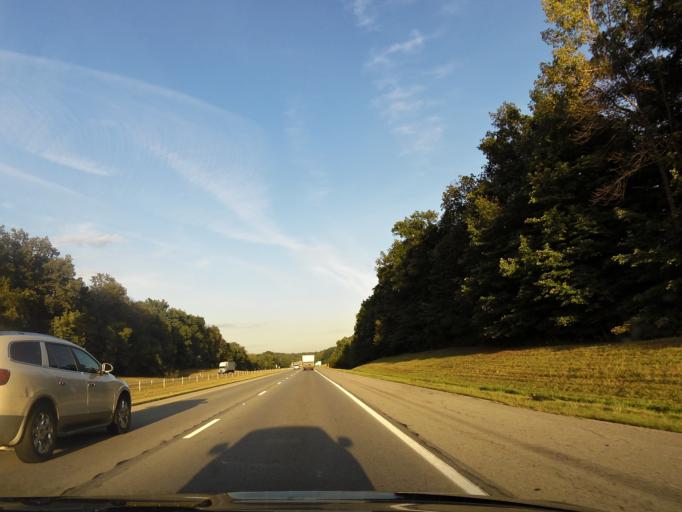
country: US
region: Indiana
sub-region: Boone County
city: Zionsville
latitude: 39.9309
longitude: -86.2932
